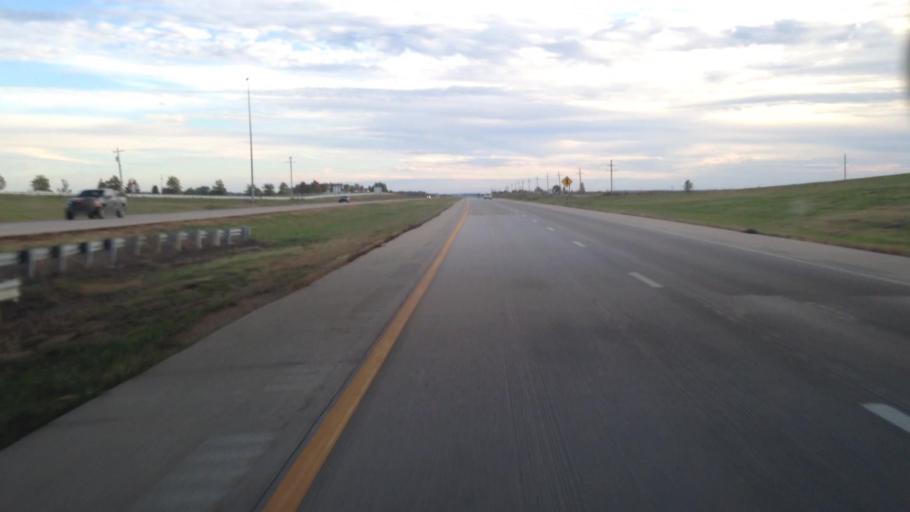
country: US
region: Kansas
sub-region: Douglas County
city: Baldwin City
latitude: 38.8333
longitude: -95.2692
